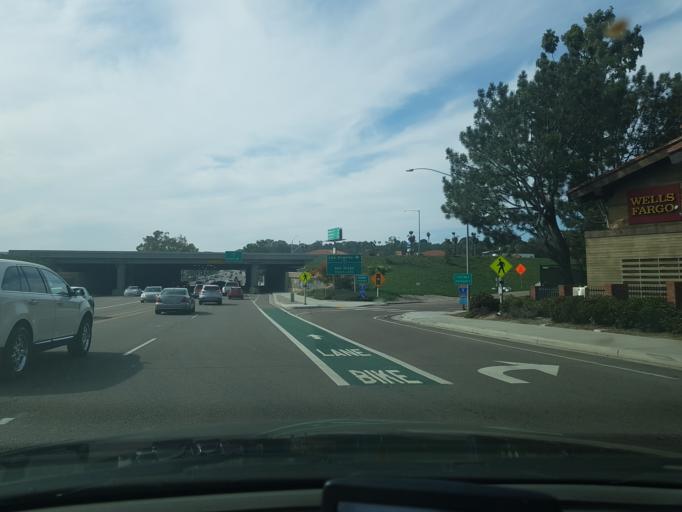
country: US
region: California
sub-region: San Diego County
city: Solana Beach
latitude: 32.9959
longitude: -117.2552
